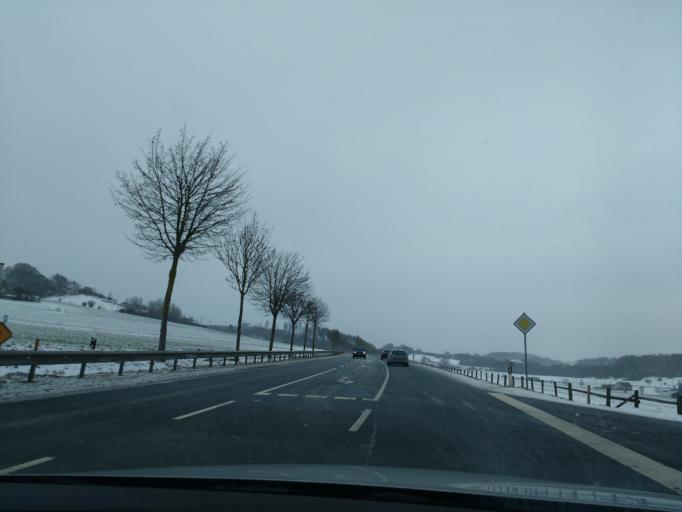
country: DE
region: North Rhine-Westphalia
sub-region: Regierungsbezirk Arnsberg
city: Brilon
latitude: 51.4030
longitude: 8.5996
